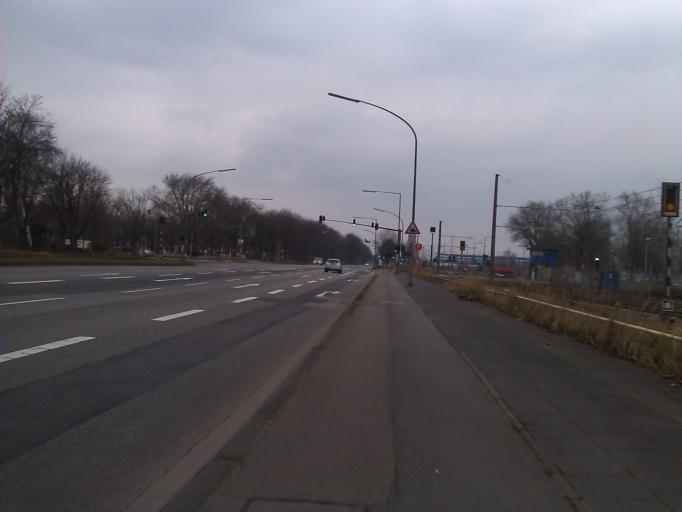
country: DE
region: North Rhine-Westphalia
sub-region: Regierungsbezirk Koln
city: Leverkusen
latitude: 51.0101
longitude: 6.9552
